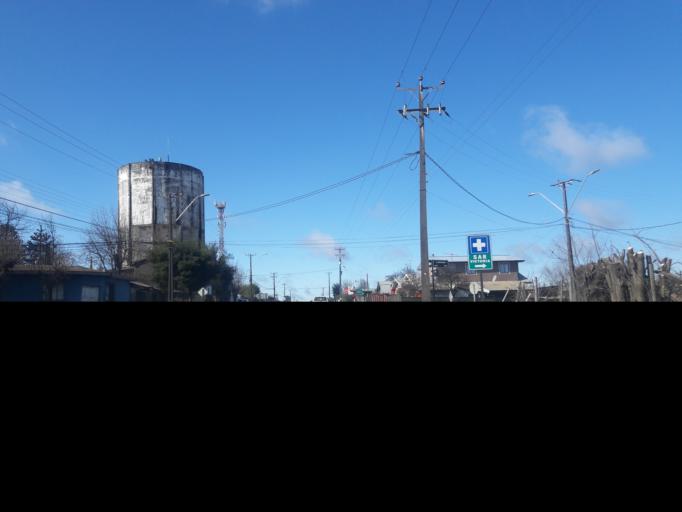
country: CL
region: Araucania
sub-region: Provincia de Malleco
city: Victoria
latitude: -38.2403
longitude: -72.3283
